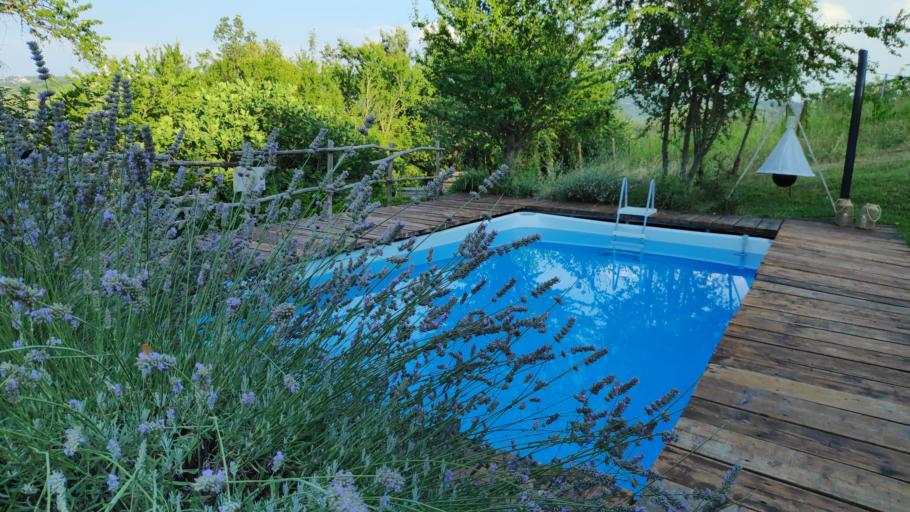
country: IT
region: Lombardy
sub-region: Provincia di Pavia
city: Montecalvo Versiggia
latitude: 44.9694
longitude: 9.2850
